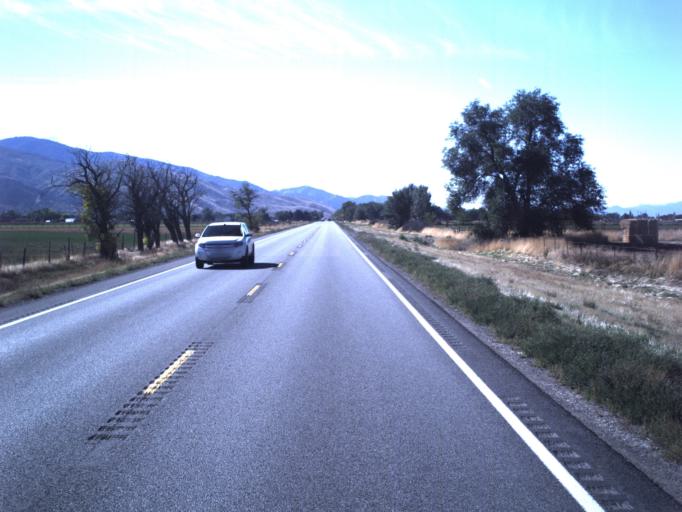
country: US
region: Utah
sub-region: Juab County
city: Nephi
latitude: 39.5721
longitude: -111.8619
